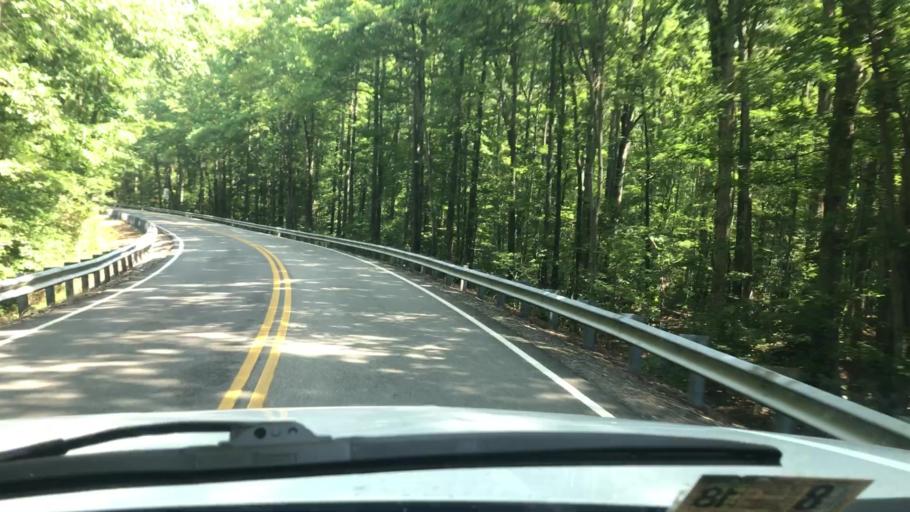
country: US
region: Virginia
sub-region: Henrico County
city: Short Pump
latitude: 37.6020
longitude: -77.6973
